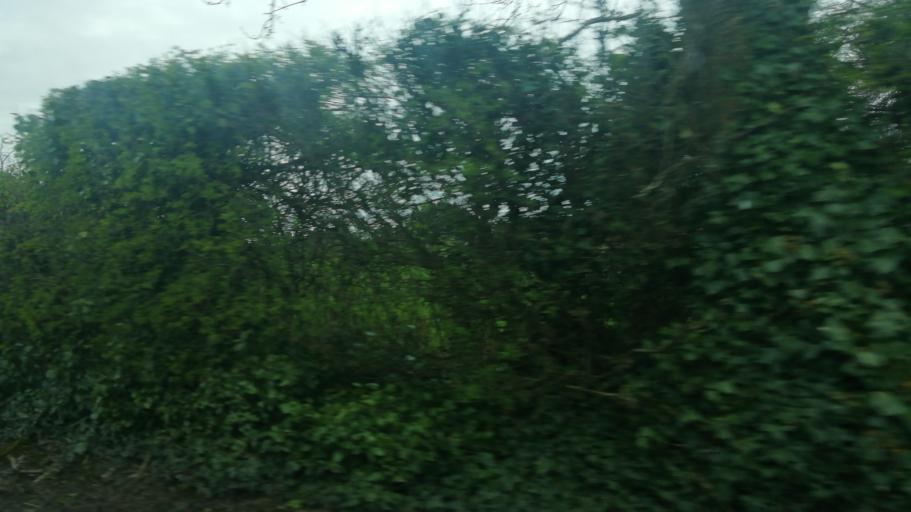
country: IE
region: Leinster
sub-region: Kildare
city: Celbridge
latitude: 53.3611
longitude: -6.5660
